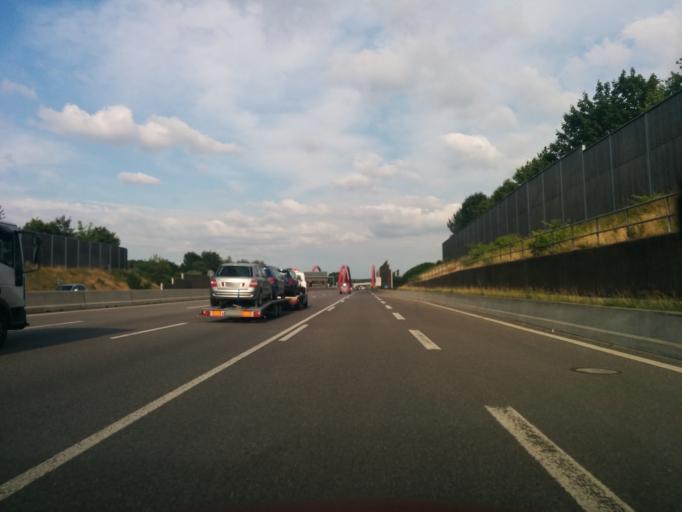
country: DE
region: Bavaria
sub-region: Swabia
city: Gersthofen
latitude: 48.4142
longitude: 10.8830
